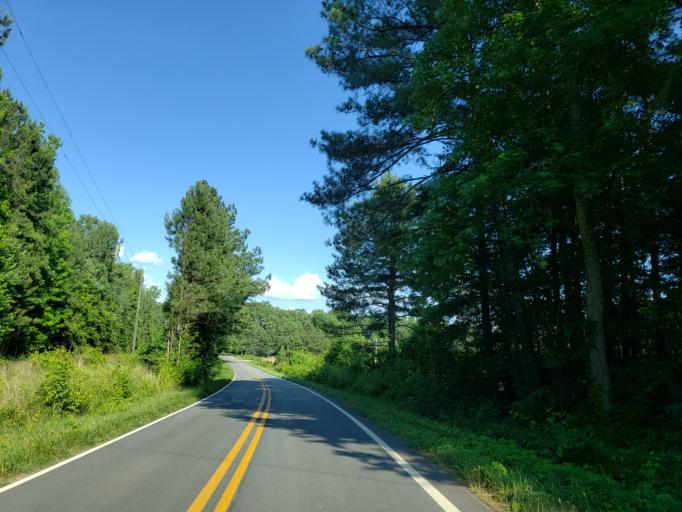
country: US
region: Georgia
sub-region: Haralson County
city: Bremen
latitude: 33.7042
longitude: -85.1078
